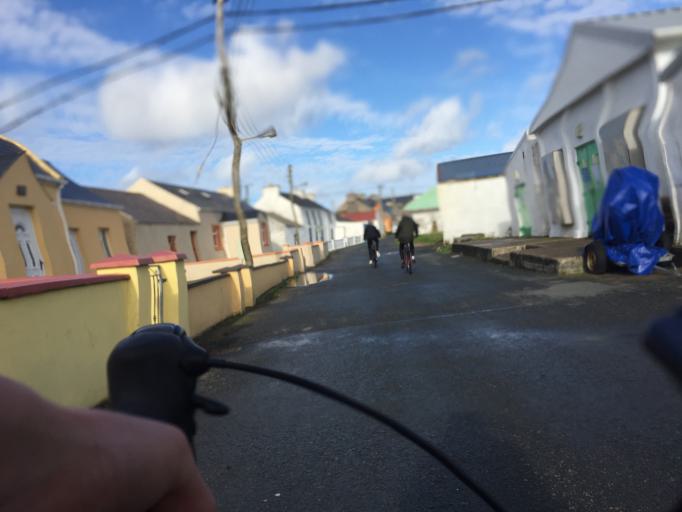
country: IE
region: Ulster
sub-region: County Donegal
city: Derrybeg
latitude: 55.2644
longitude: -8.2285
